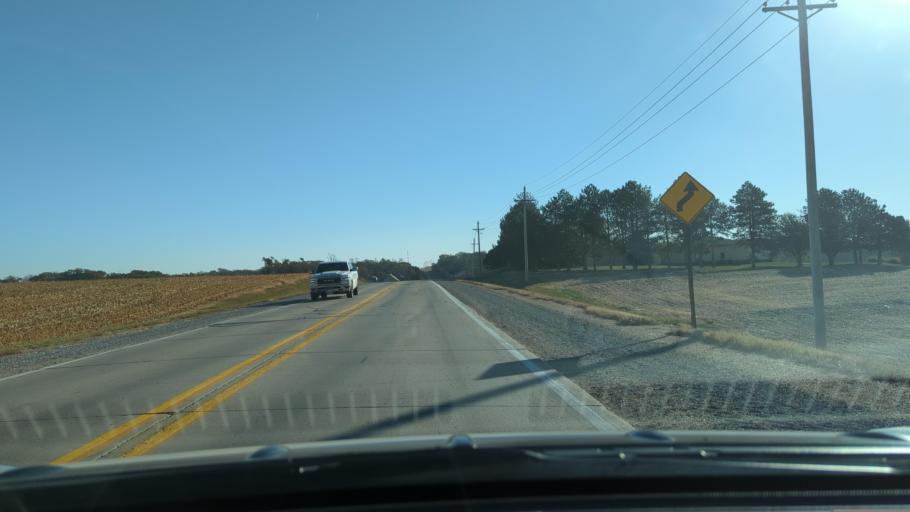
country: US
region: Nebraska
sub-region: Sarpy County
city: Papillion
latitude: 41.0928
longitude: -95.9975
